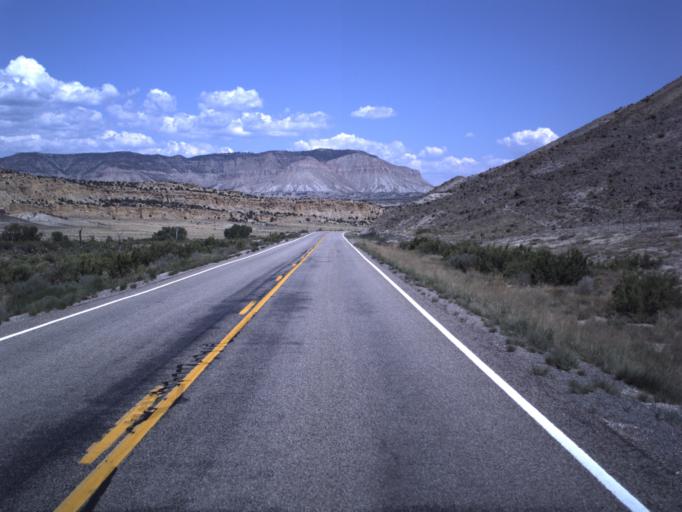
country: US
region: Utah
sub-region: Emery County
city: Ferron
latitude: 38.7788
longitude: -111.3497
